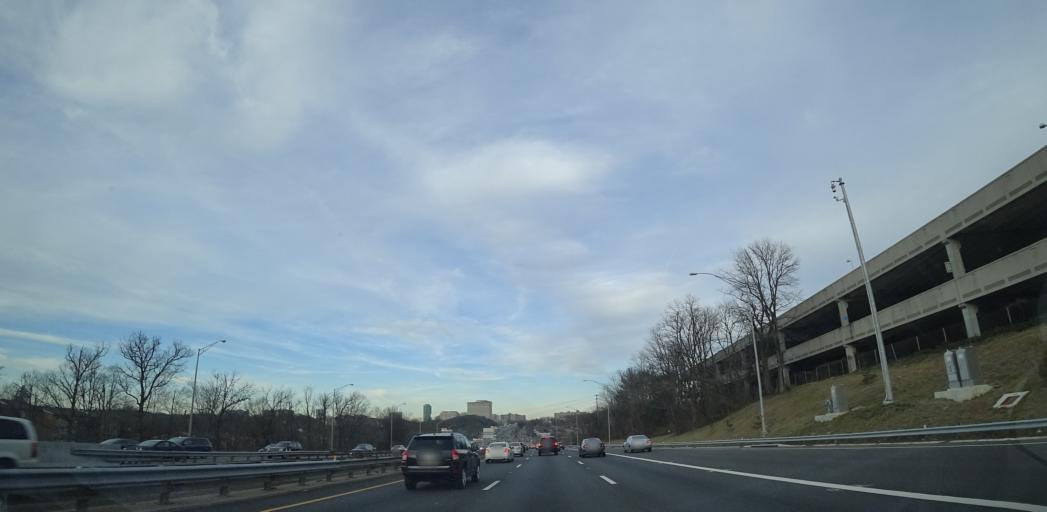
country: US
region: Virginia
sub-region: Fairfax County
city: Lincolnia
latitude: 38.8182
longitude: -77.1317
